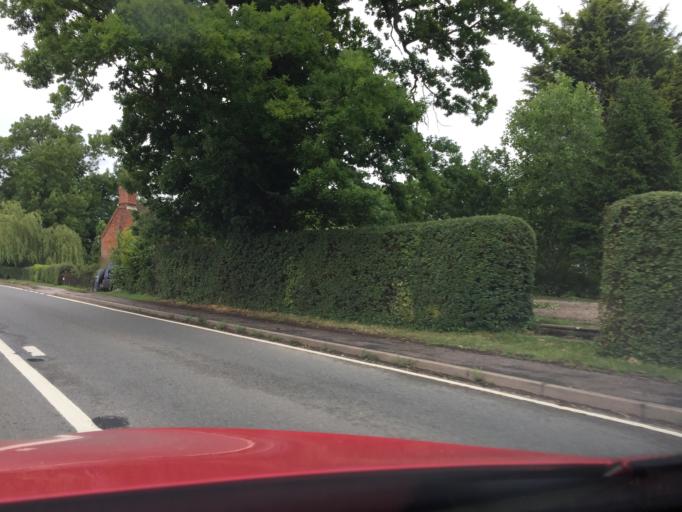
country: GB
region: England
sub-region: Warwickshire
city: Dunchurch
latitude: 52.2588
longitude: -1.2817
